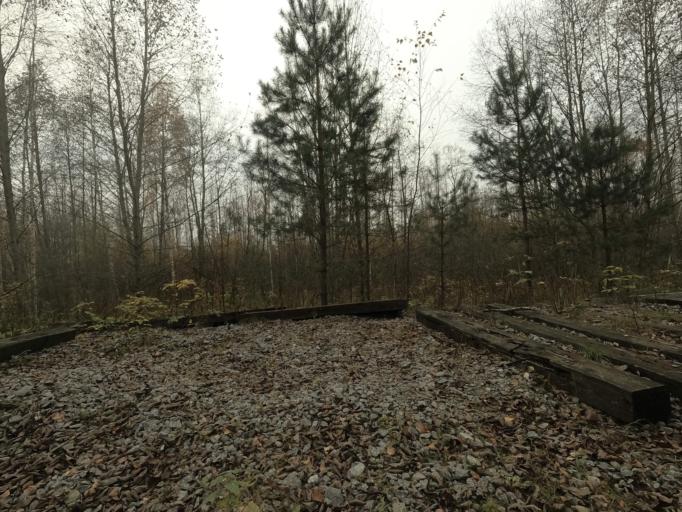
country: RU
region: Leningrad
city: Kirovsk
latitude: 59.8591
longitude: 30.9976
